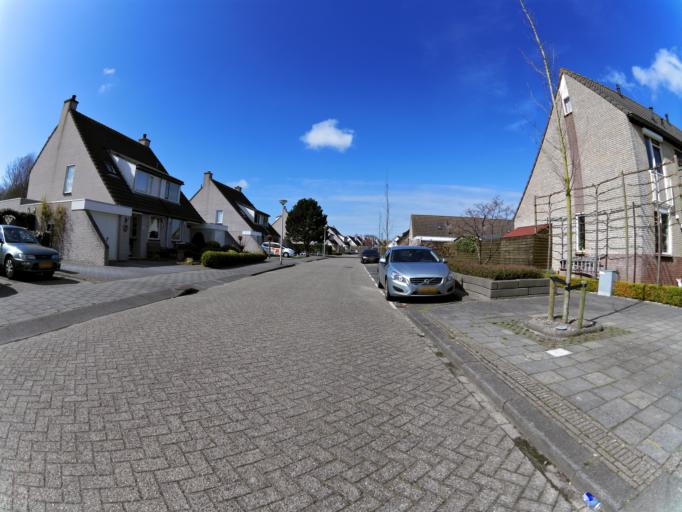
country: NL
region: South Holland
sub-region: Gemeente Hellevoetsluis
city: Nieuw-Helvoet
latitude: 51.8680
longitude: 4.0658
